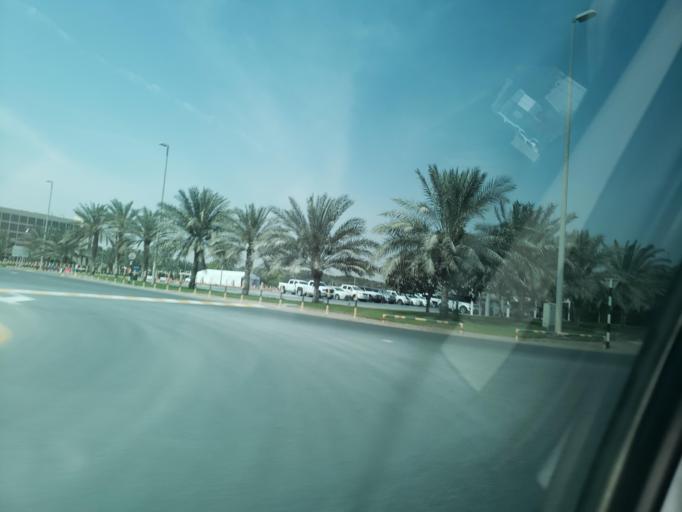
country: AE
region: Ash Shariqah
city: Sharjah
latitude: 25.3212
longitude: 55.5159
